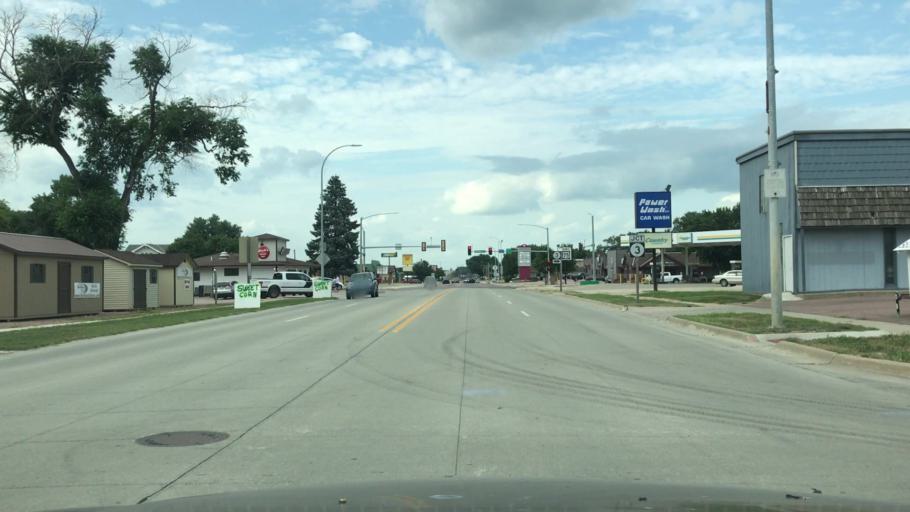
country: US
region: Iowa
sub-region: Plymouth County
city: Le Mars
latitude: 42.7919
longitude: -96.1738
